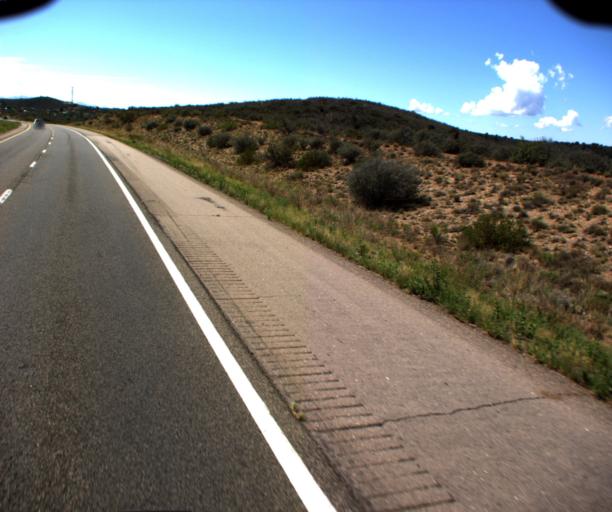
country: US
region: Arizona
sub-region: Yavapai County
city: Mayer
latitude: 34.4098
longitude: -112.2436
